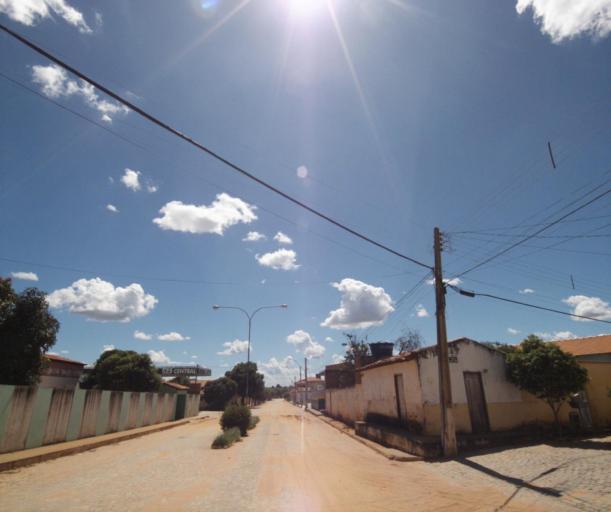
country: BR
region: Bahia
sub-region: Carinhanha
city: Carinhanha
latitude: -14.2118
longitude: -44.2796
